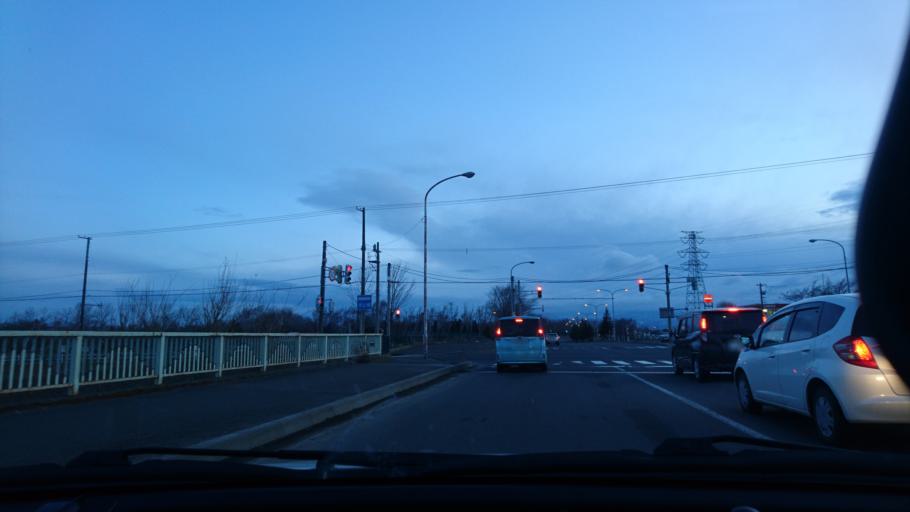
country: JP
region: Hokkaido
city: Sapporo
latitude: 43.1233
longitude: 141.4143
